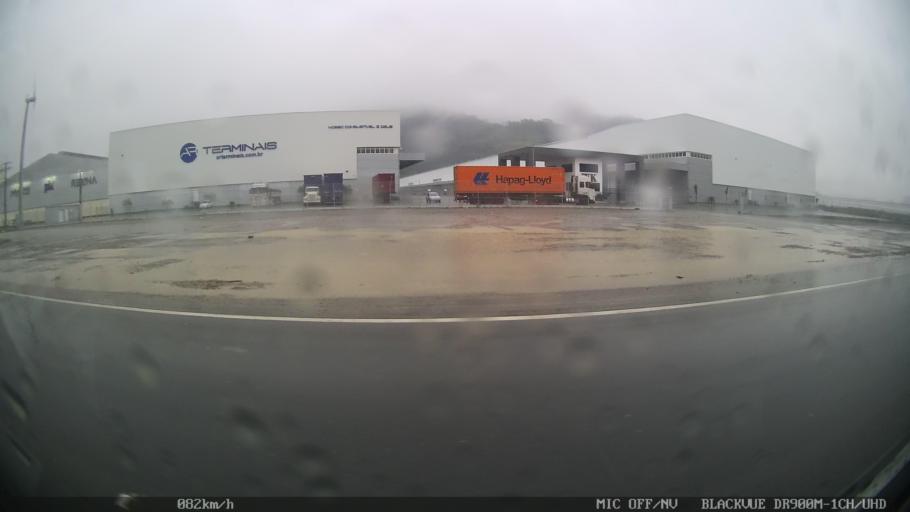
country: BR
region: Santa Catarina
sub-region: Navegantes
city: Navegantes
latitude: -26.8542
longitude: -48.7052
